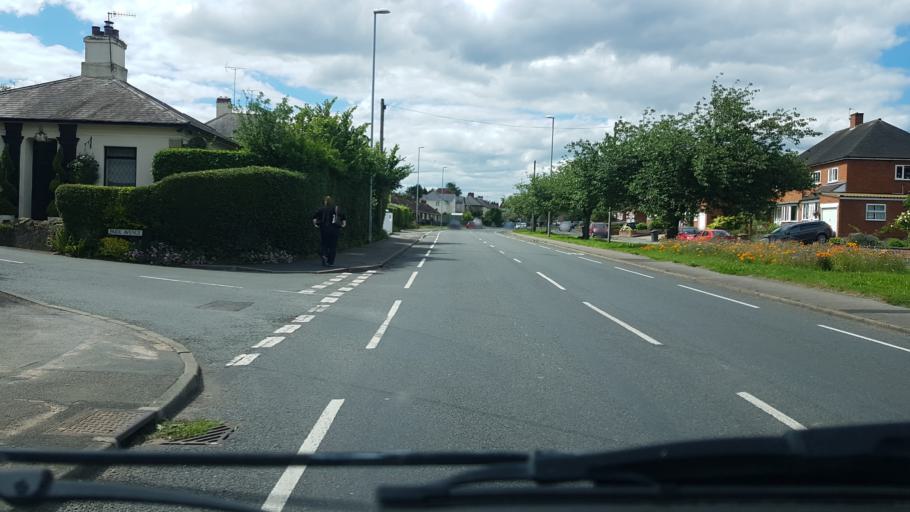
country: GB
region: England
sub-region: Worcestershire
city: Stourport-on-Severn
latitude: 52.3448
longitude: -2.2797
